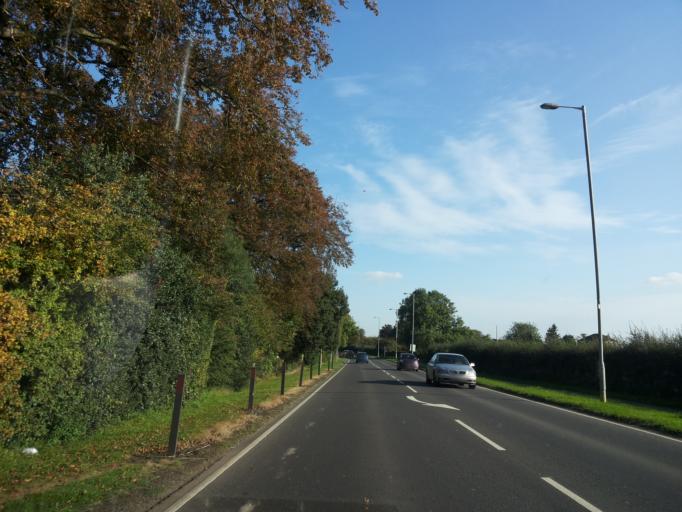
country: GB
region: England
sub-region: East Riding of Yorkshire
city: Snaith
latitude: 53.6899
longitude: -1.0209
